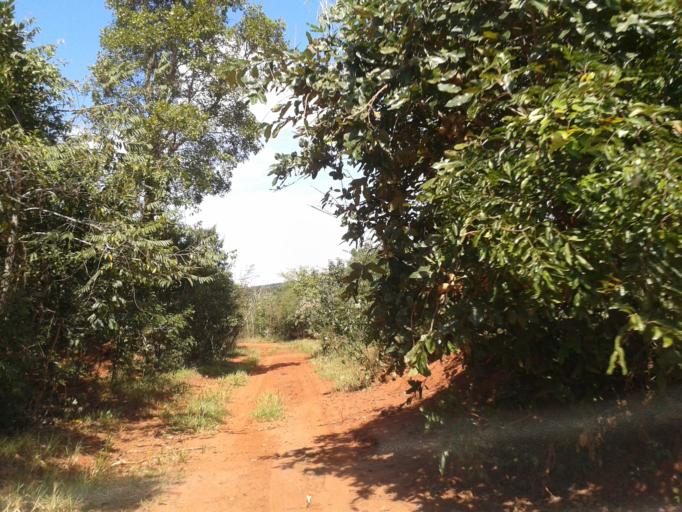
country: BR
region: Minas Gerais
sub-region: Campina Verde
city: Campina Verde
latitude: -19.4382
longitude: -49.7042
